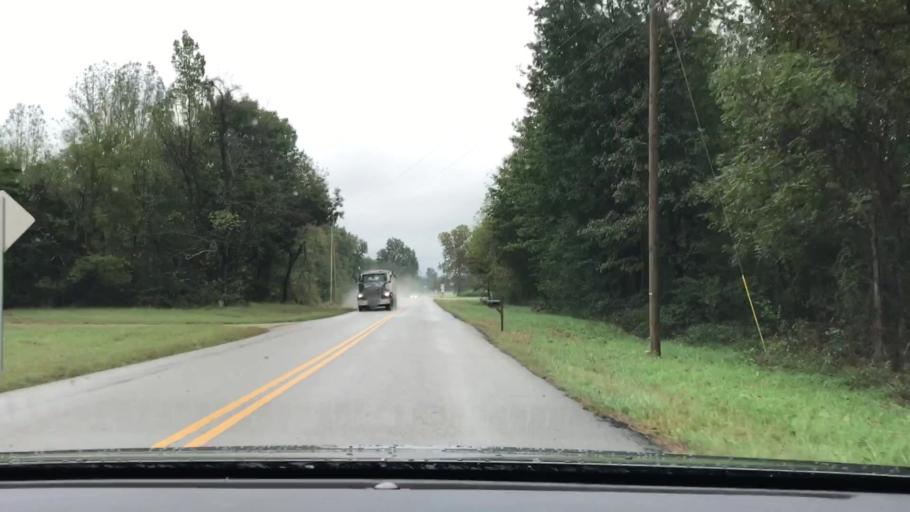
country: US
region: Kentucky
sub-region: McLean County
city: Calhoun
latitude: 37.4743
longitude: -87.2426
